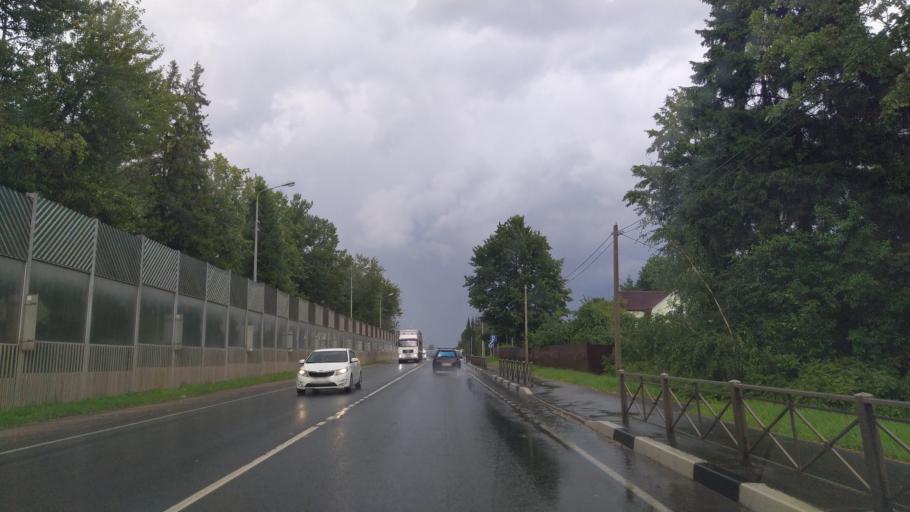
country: RU
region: Pskov
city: Pskov
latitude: 57.7568
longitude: 28.3824
